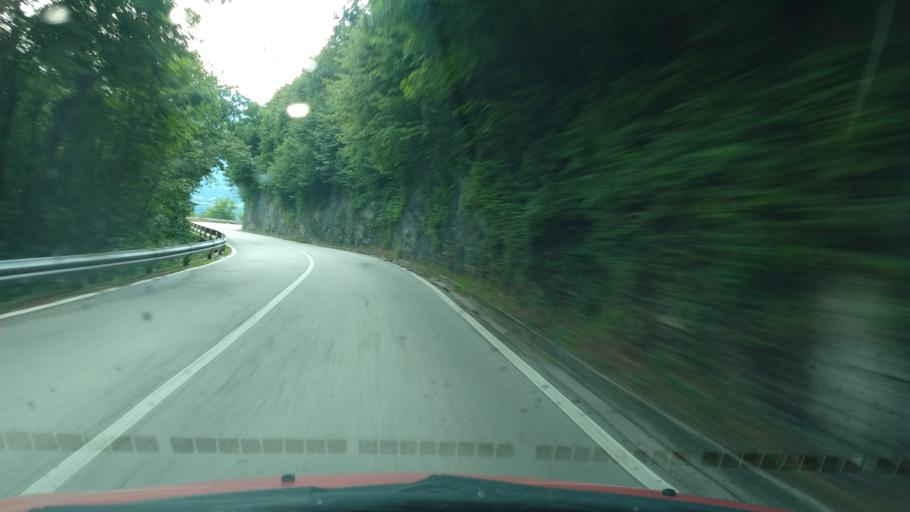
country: IT
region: Veneto
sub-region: Provincia di Vicenza
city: Arsiero
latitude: 45.8287
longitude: 11.3633
